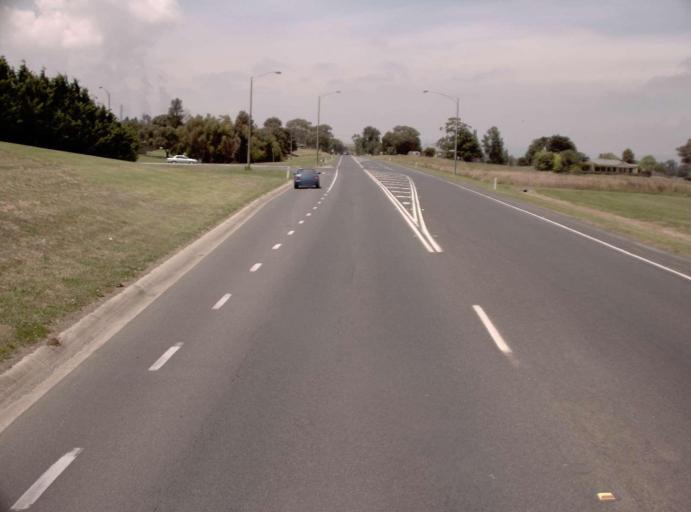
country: AU
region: Victoria
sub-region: Latrobe
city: Traralgon
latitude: -38.2076
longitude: 146.5444
